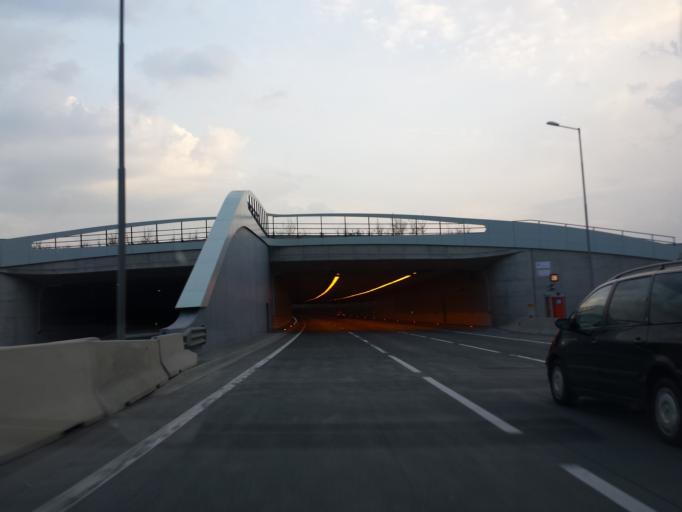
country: AT
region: Lower Austria
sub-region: Politischer Bezirk Mistelbach
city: Grossebersdorf
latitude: 48.3622
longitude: 16.4836
